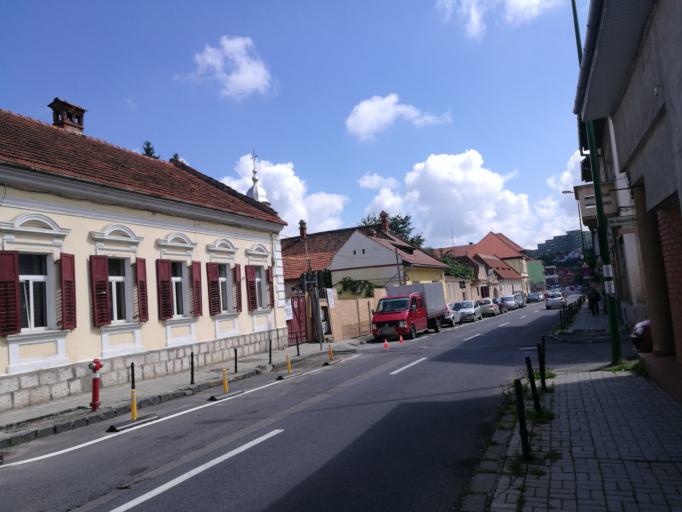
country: RO
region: Brasov
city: Brasov
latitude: 45.6537
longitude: 25.5888
